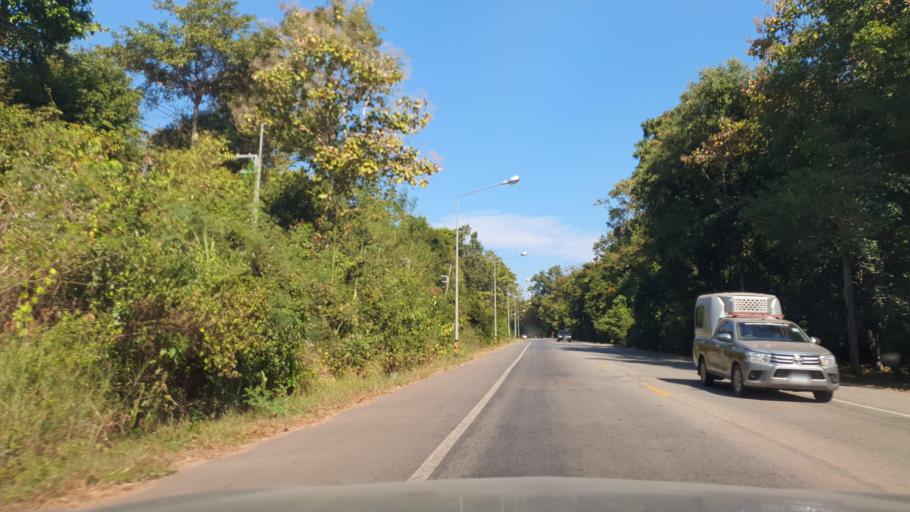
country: TH
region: Sakon Nakhon
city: Phu Phan
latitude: 17.0994
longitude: 103.9916
